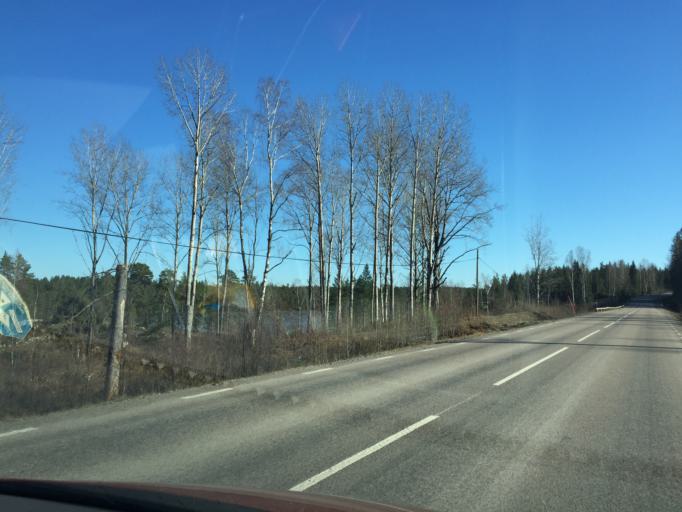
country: SE
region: OEstergoetland
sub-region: Finspangs Kommun
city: Finspang
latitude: 58.7705
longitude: 15.7961
